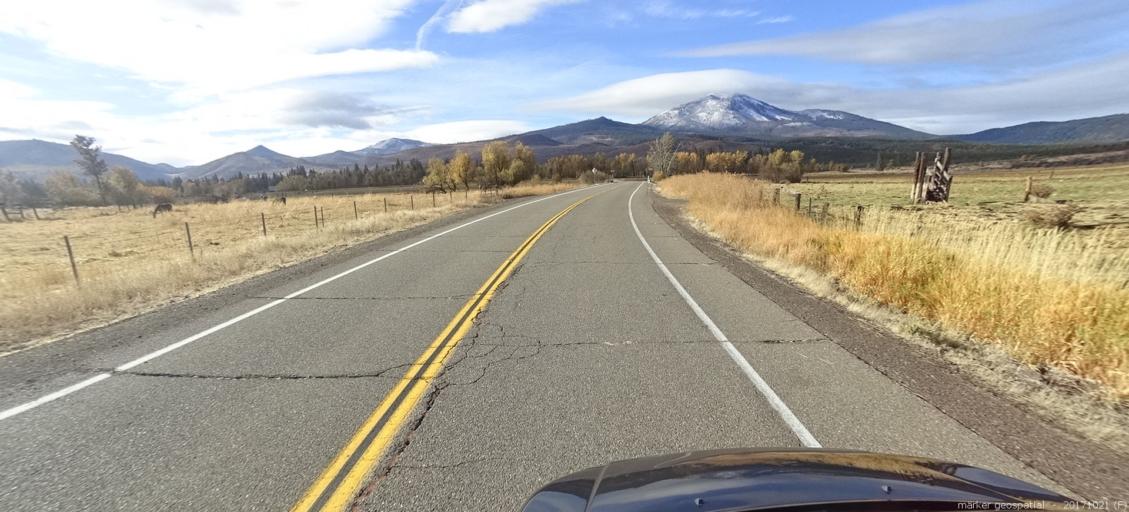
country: US
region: California
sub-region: Shasta County
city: Burney
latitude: 40.8807
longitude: -121.5573
